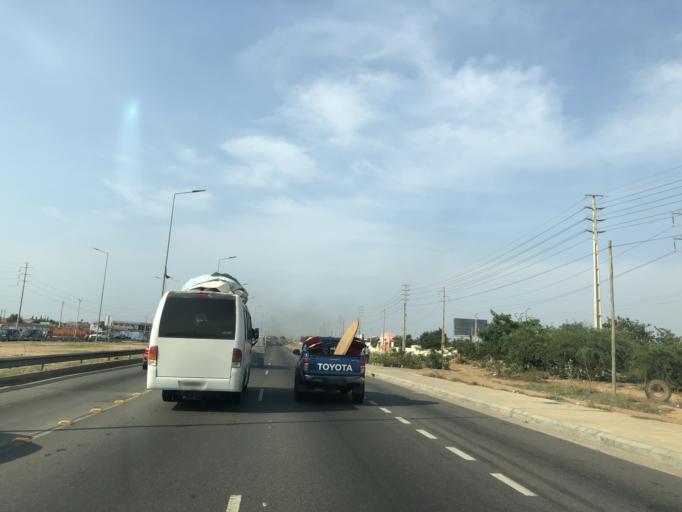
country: AO
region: Luanda
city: Luanda
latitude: -8.9471
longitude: 13.2601
